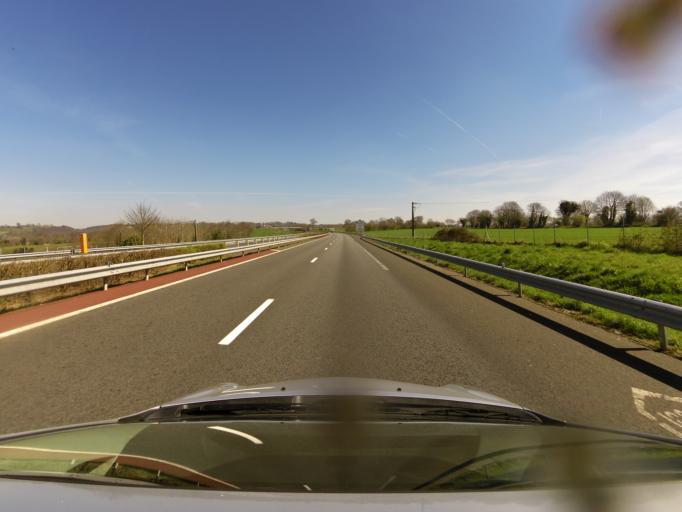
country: FR
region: Lower Normandy
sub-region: Departement de la Manche
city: Saint-Senier-sous-Avranches
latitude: 48.7144
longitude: -1.3235
